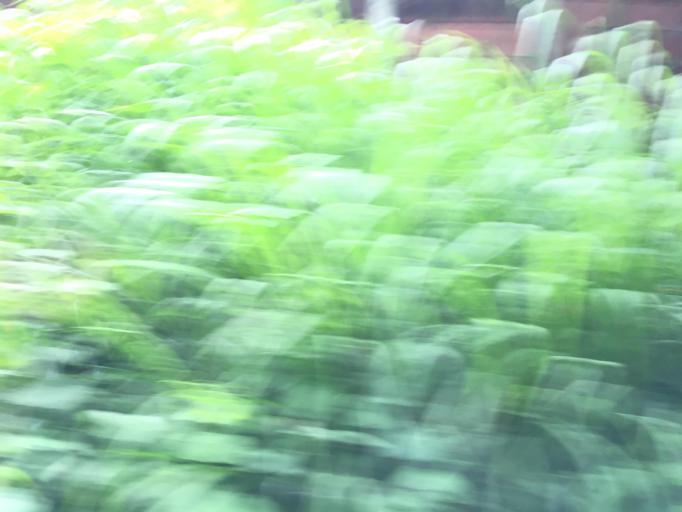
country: GT
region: Guatemala
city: Amatitlan
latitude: 14.4998
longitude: -90.6156
